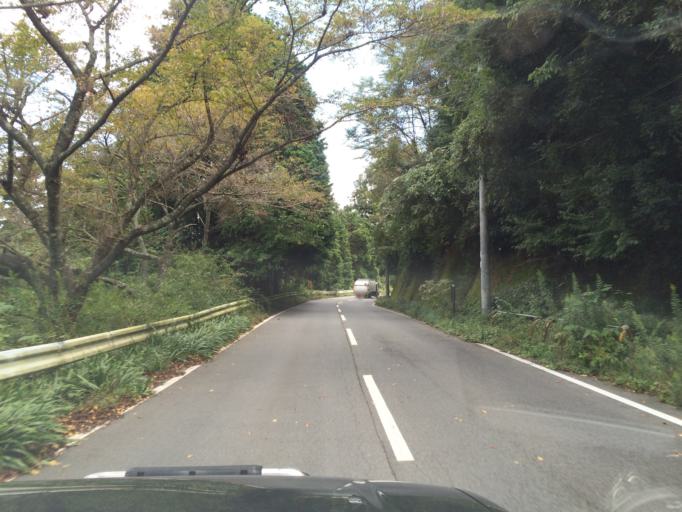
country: JP
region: Mie
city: Nabari
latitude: 34.6778
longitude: 135.9570
